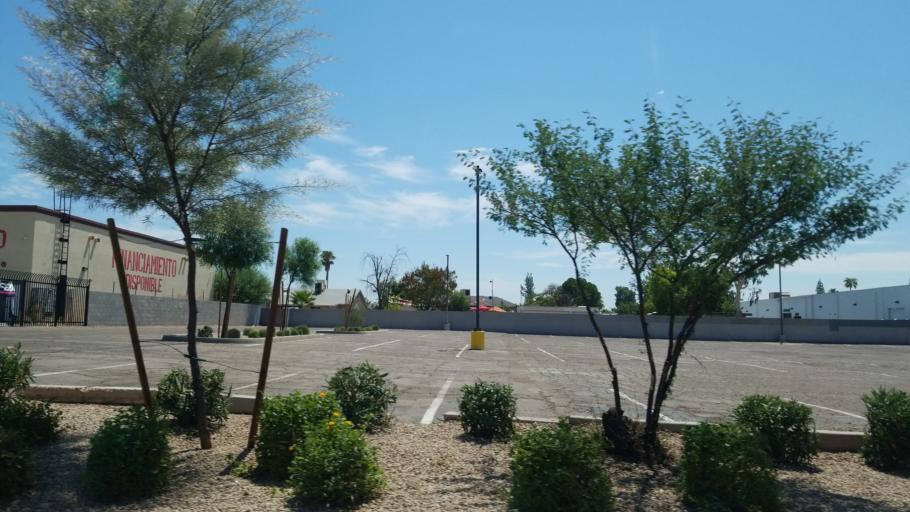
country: US
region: Arizona
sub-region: Maricopa County
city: Glendale
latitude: 33.5116
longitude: -112.1514
